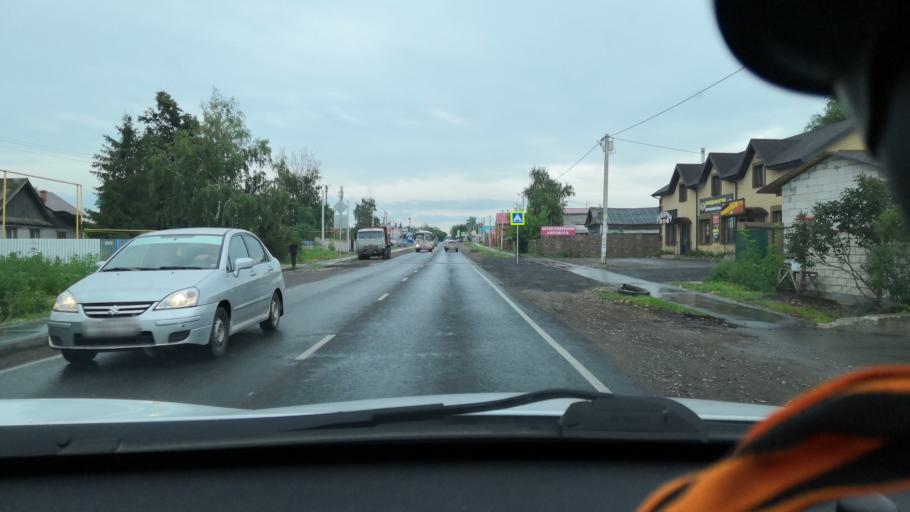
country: RU
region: Samara
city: Novosemeykino
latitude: 53.3775
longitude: 50.3449
